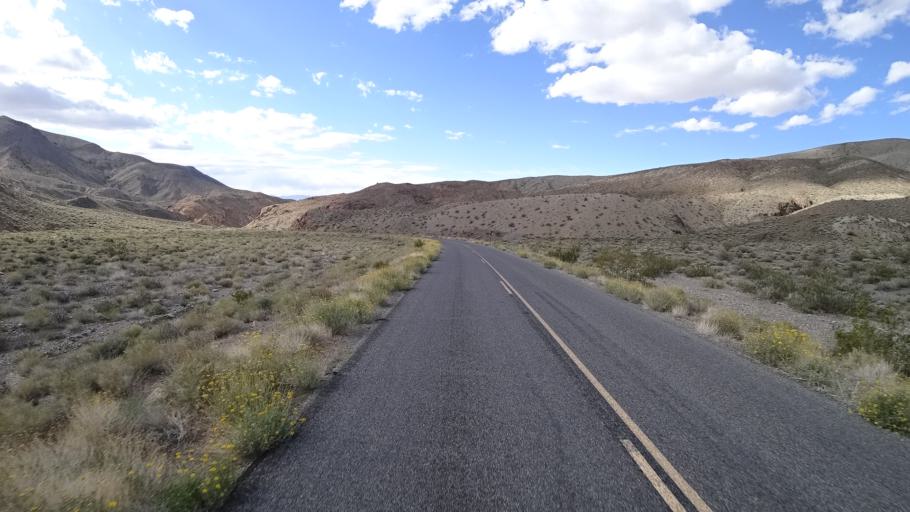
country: US
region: Nevada
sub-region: Nye County
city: Beatty
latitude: 36.4210
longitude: -117.1876
